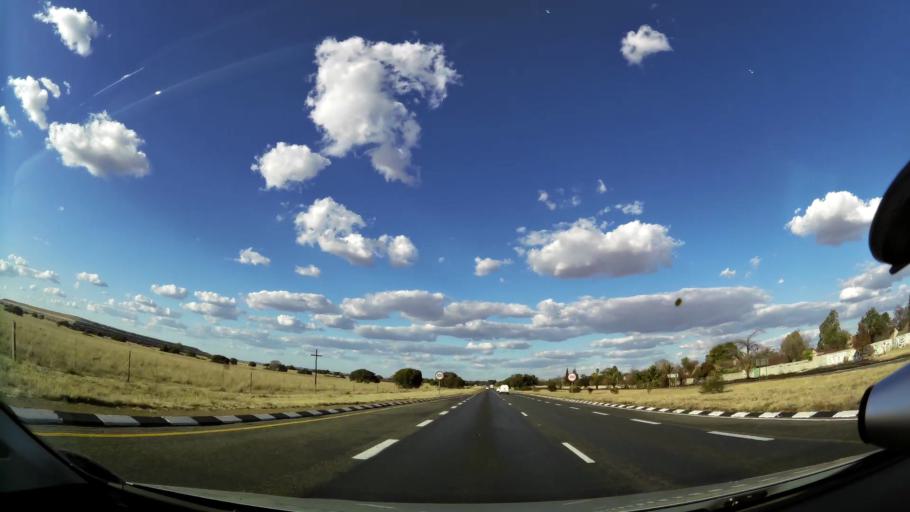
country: ZA
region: North-West
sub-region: Dr Kenneth Kaunda District Municipality
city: Stilfontein
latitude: -26.8404
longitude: 26.7591
